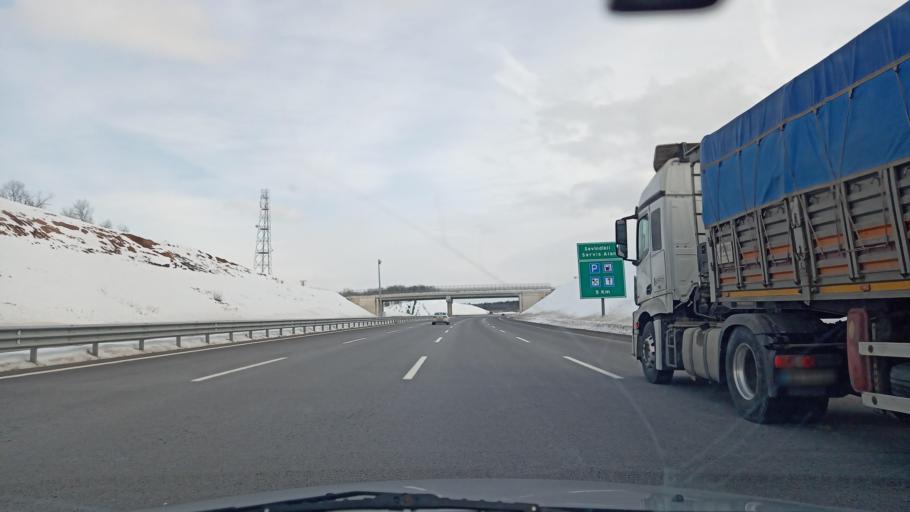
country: TR
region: Kocaeli
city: Hereke
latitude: 40.8990
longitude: 29.6408
